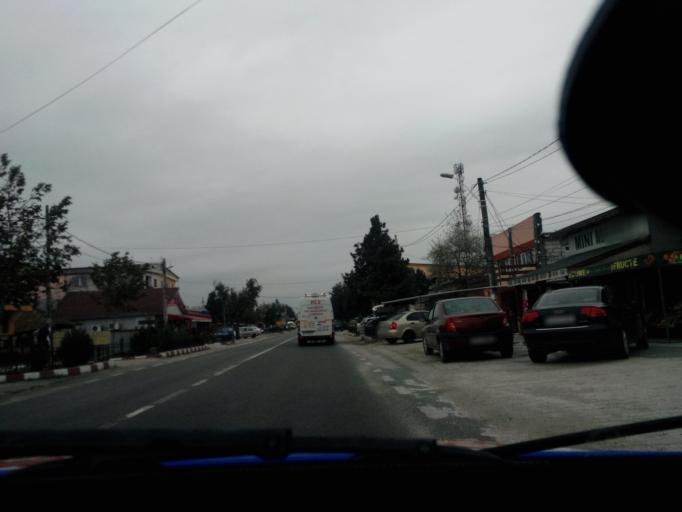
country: RO
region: Giurgiu
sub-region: Comuna Mihailesti
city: Mihailesti
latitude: 44.3229
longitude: 25.9061
